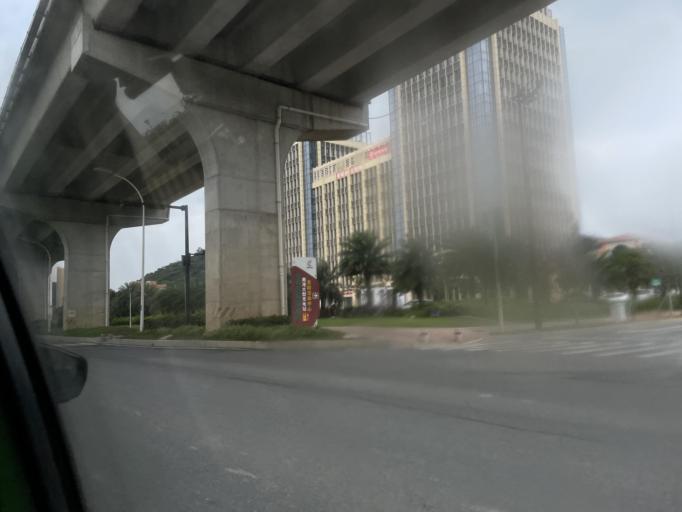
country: CN
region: Guangdong
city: Wanzai
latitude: 22.1765
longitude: 113.4836
